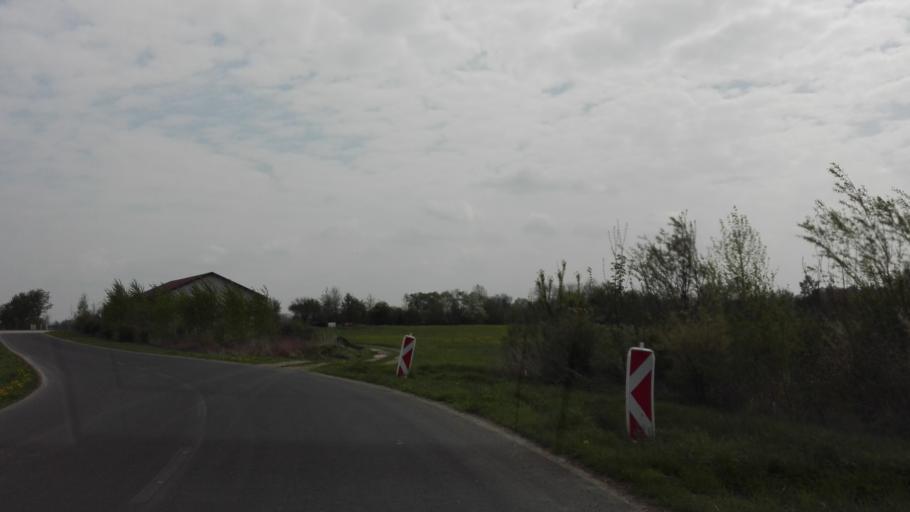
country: AT
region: Upper Austria
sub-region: Politischer Bezirk Perg
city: Perg
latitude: 48.2219
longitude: 14.6974
